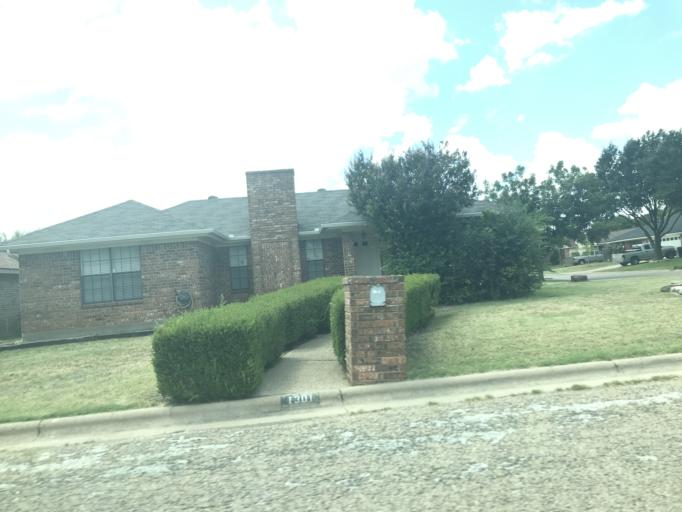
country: US
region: Texas
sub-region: Taylor County
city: Abilene
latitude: 32.4435
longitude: -99.7022
